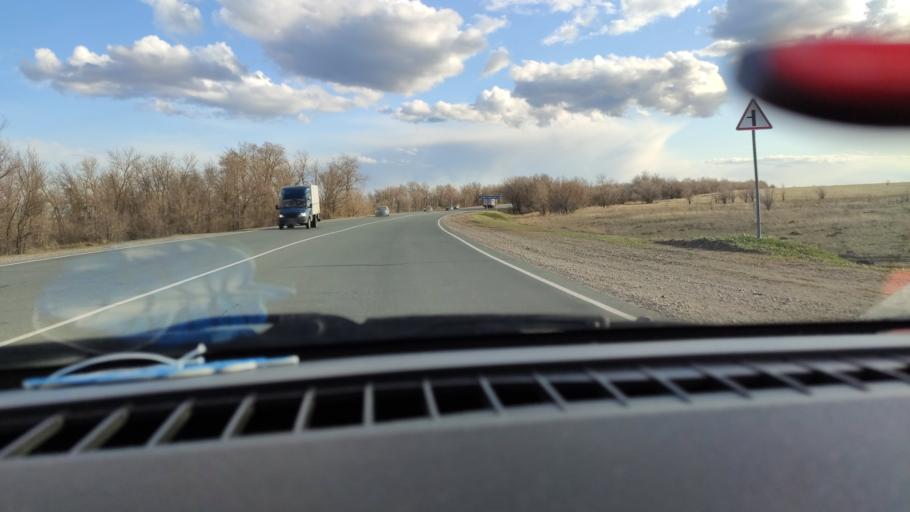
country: RU
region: Saratov
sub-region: Saratovskiy Rayon
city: Saratov
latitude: 51.7133
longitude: 46.0224
